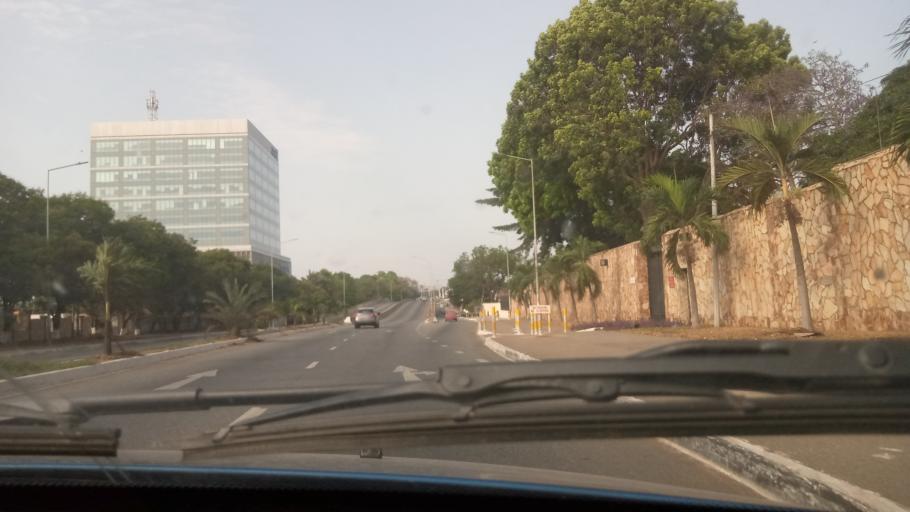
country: GH
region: Greater Accra
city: Accra
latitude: 5.5699
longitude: -0.1914
